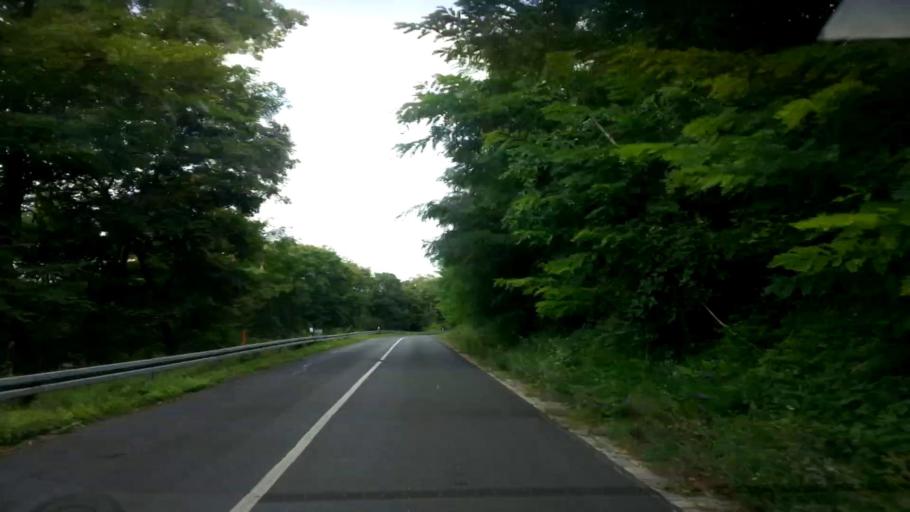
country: DE
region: Bavaria
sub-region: Regierungsbezirk Unterfranken
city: Rodelsee
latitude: 49.7260
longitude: 10.2703
